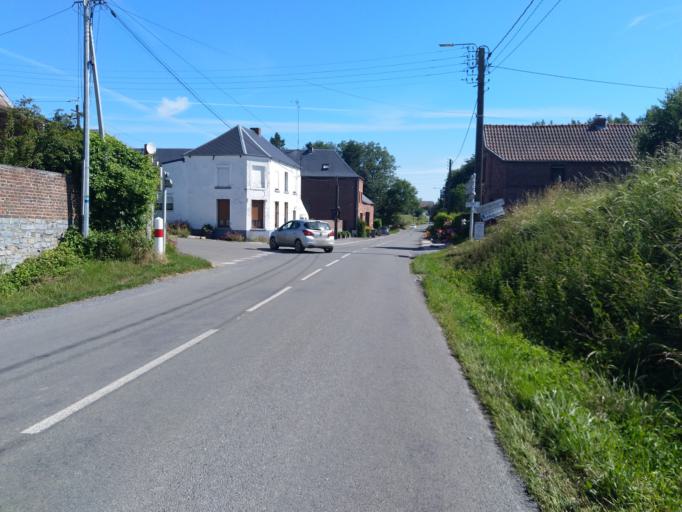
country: FR
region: Nord-Pas-de-Calais
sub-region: Departement du Nord
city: Bavay
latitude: 50.3237
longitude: 3.8249
